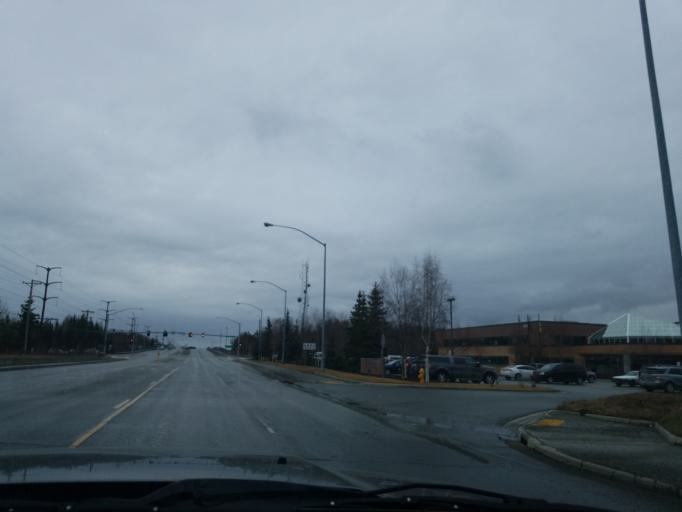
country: US
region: Alaska
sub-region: Anchorage Municipality
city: Anchorage
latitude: 61.1786
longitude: -149.8083
